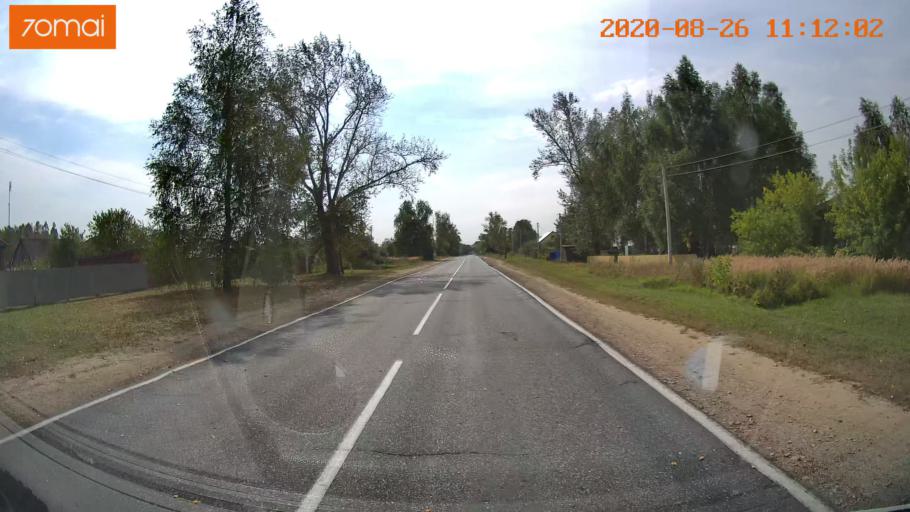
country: RU
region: Rjazan
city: Izhevskoye
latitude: 54.4745
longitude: 41.1257
